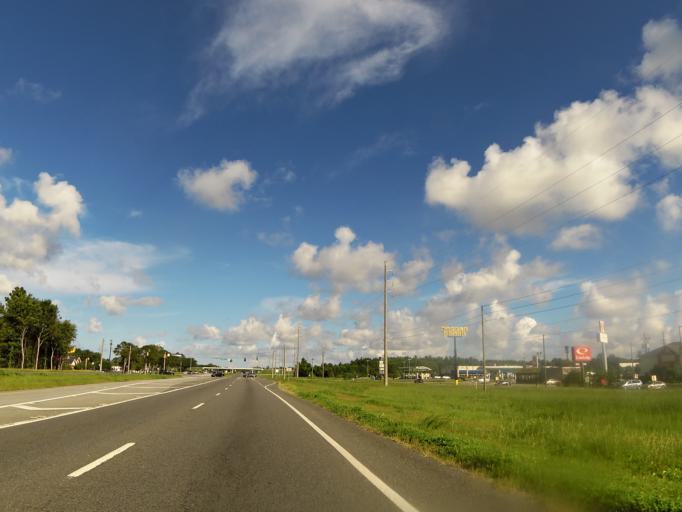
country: US
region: Georgia
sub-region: Glynn County
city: Dock Junction
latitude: 31.1403
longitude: -81.5818
